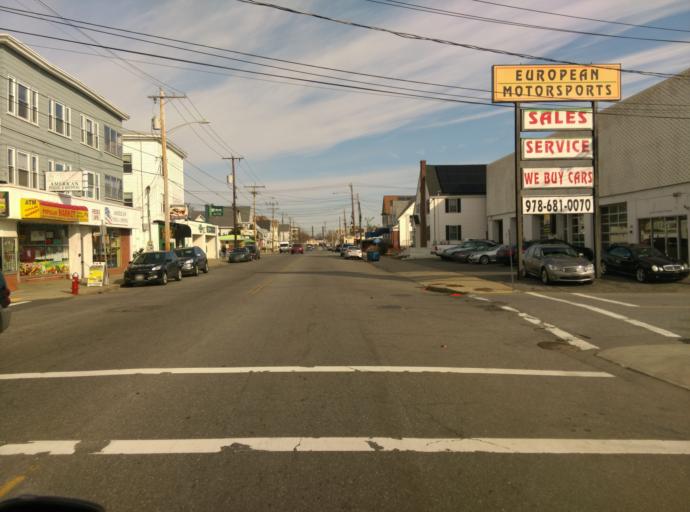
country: US
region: Massachusetts
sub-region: Essex County
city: Lawrence
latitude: 42.6899
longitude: -71.1591
